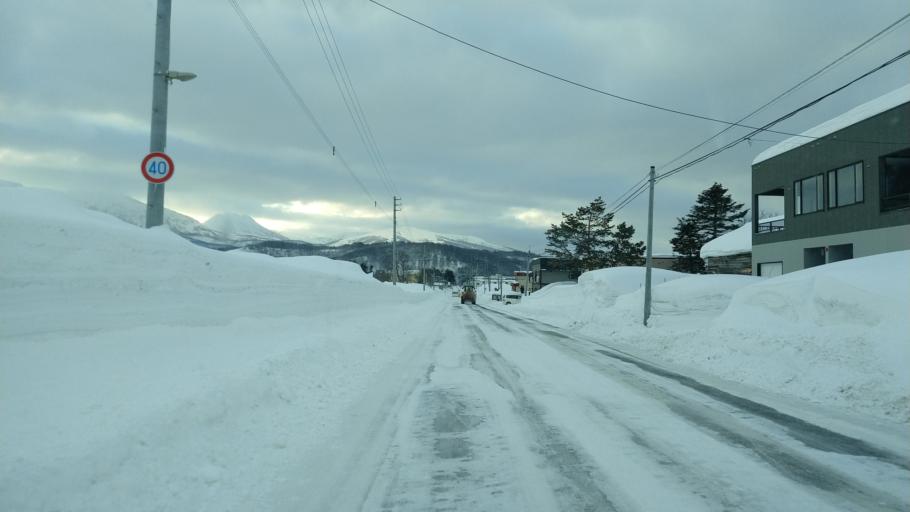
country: JP
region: Hokkaido
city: Niseko Town
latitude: 42.9085
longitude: 140.7623
